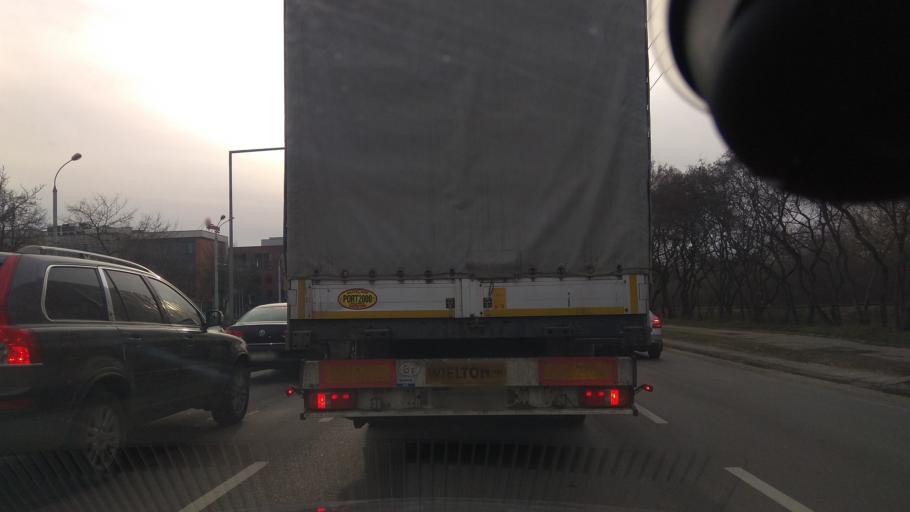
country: LT
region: Vilnius County
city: Lazdynai
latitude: 54.6527
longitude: 25.2267
